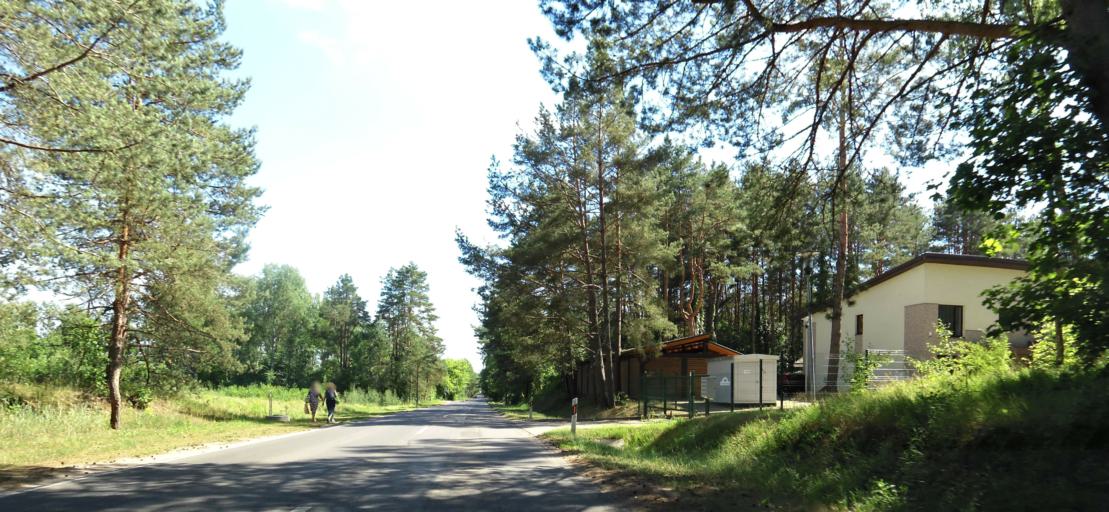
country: LT
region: Vilnius County
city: Rasos
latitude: 54.7971
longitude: 25.3494
